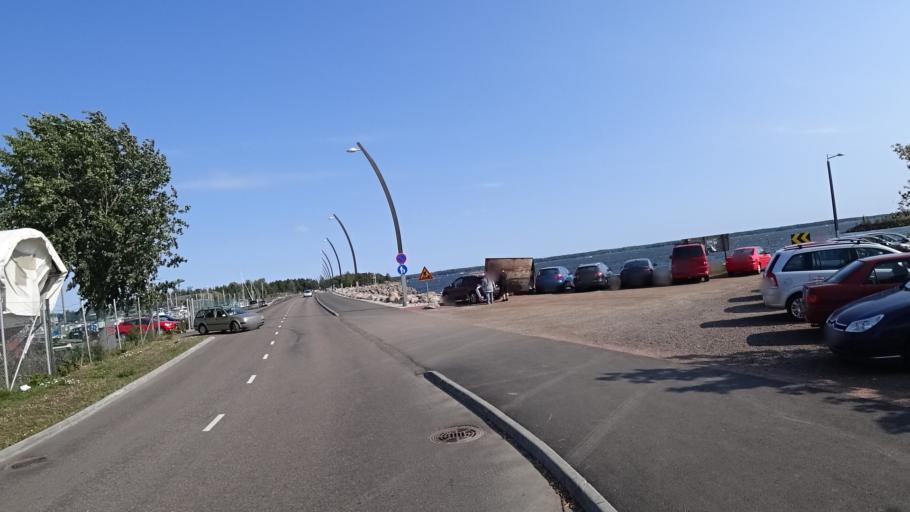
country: FI
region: Kymenlaakso
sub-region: Kotka-Hamina
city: Kotka
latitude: 60.4588
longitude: 26.9554
